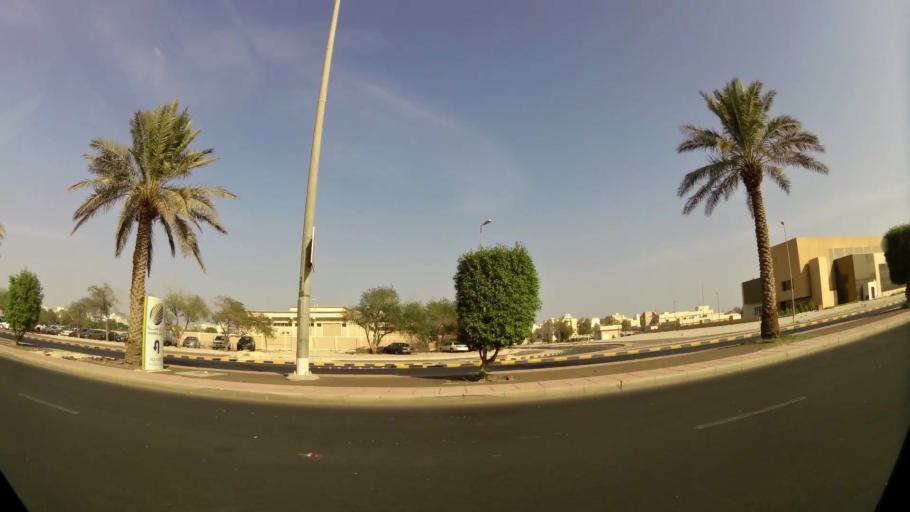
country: KW
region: Mubarak al Kabir
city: Mubarak al Kabir
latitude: 29.1730
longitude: 48.0998
